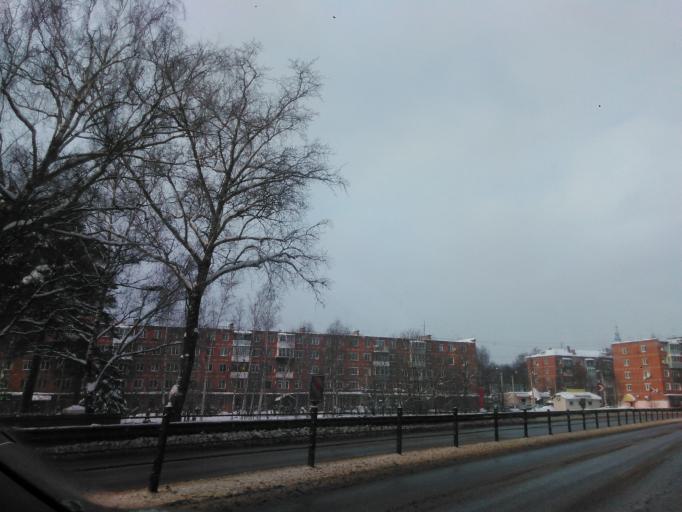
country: RU
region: Moskovskaya
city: Dedenevo
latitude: 56.2369
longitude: 37.5239
